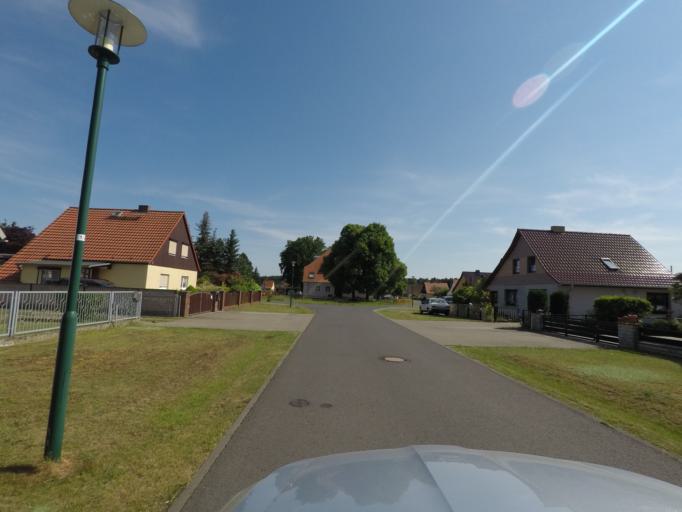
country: DE
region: Brandenburg
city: Melchow
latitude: 52.8640
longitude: 13.7185
